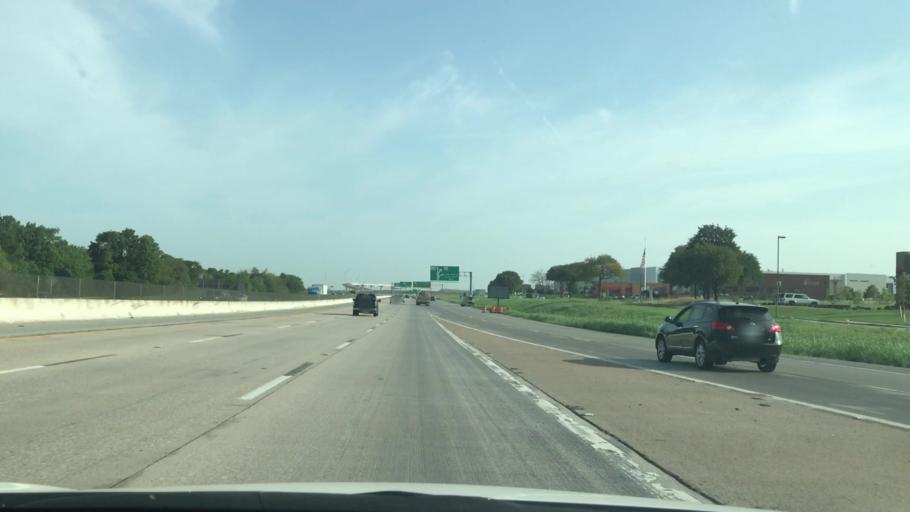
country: US
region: Texas
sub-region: Tarrant County
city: Euless
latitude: 32.8249
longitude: -97.0610
